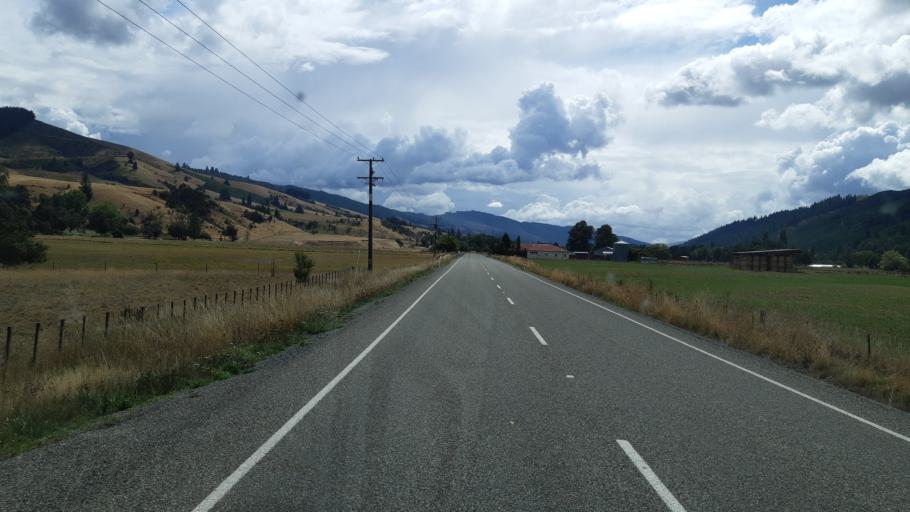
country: NZ
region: Tasman
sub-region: Tasman District
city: Wakefield
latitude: -41.5173
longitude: 172.7956
